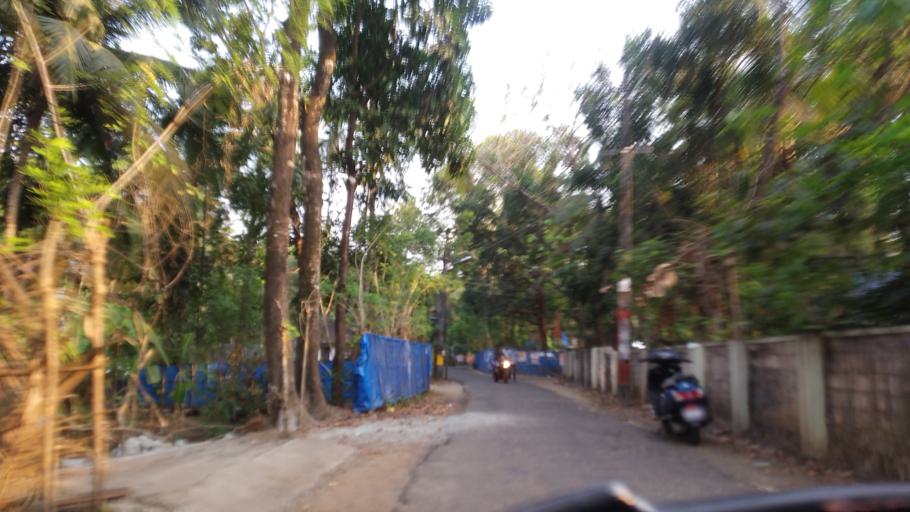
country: IN
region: Kerala
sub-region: Thrissur District
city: Thanniyam
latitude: 10.4188
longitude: 76.0856
